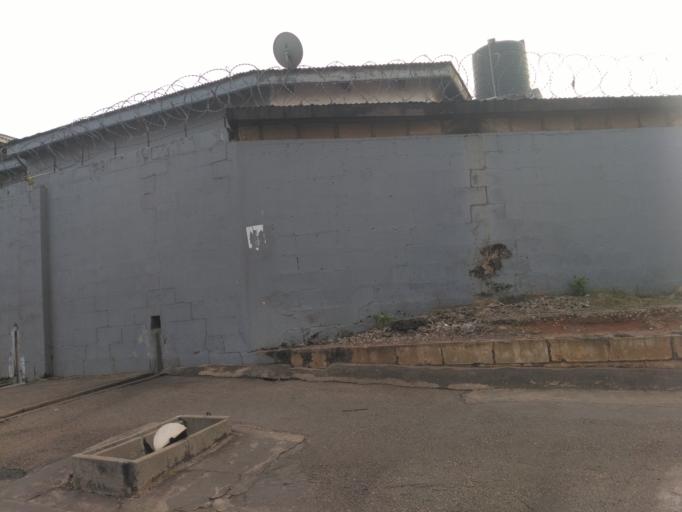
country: GH
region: Ashanti
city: Kumasi
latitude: 6.6861
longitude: -1.6221
